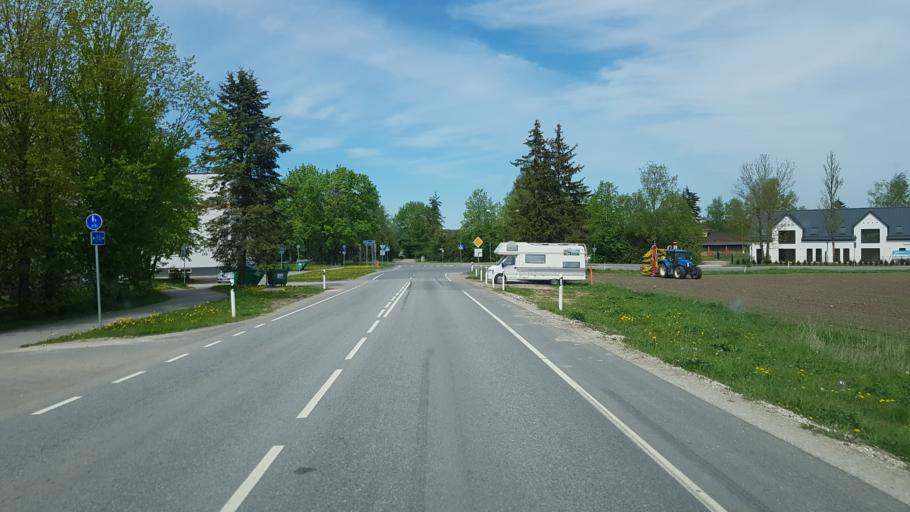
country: EE
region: Tartu
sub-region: Noo vald
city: Noo
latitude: 58.3864
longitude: 26.5621
